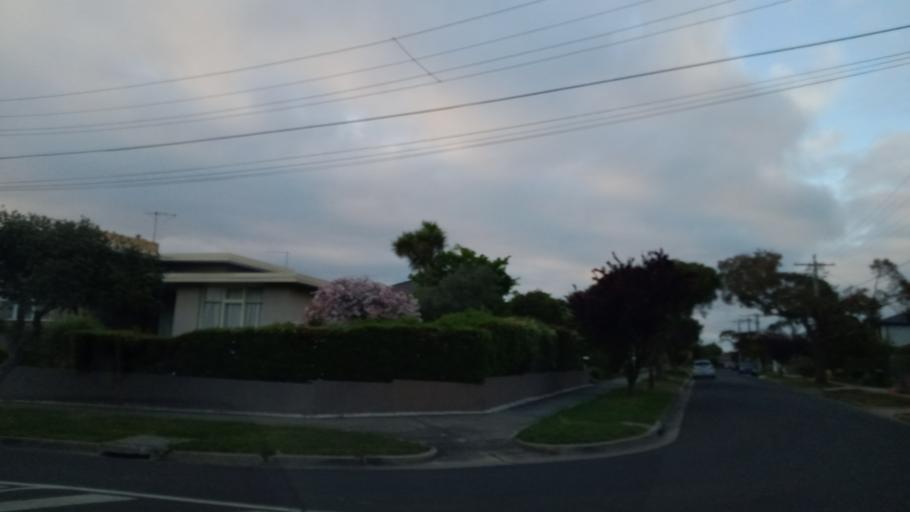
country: AU
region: Victoria
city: Burwood East
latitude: -37.8731
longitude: 145.1409
